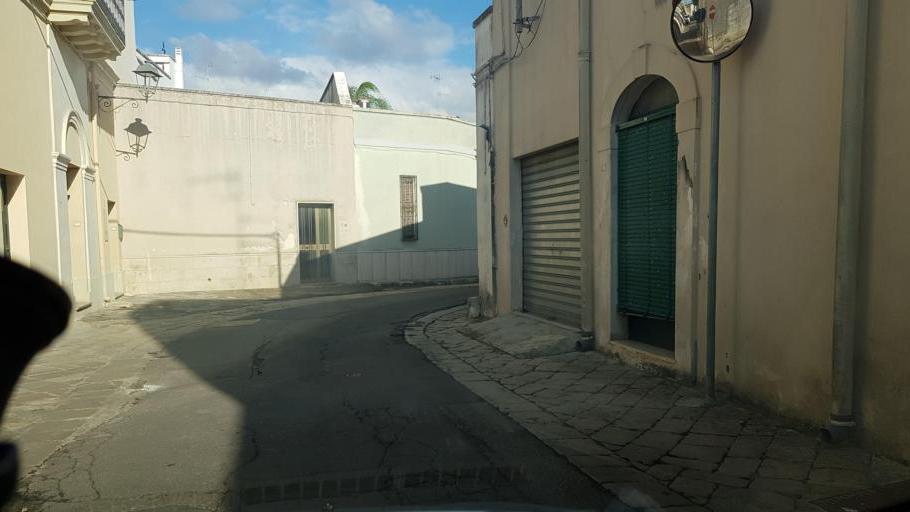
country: IT
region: Apulia
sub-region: Provincia di Lecce
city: Campi Salentina
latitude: 40.4004
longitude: 18.0176
